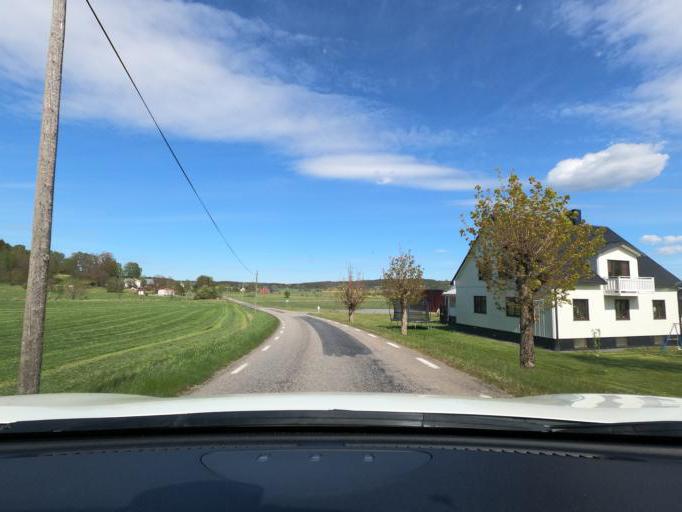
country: SE
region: Vaestra Goetaland
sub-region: Marks Kommun
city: Horred
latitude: 57.4494
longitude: 12.4782
